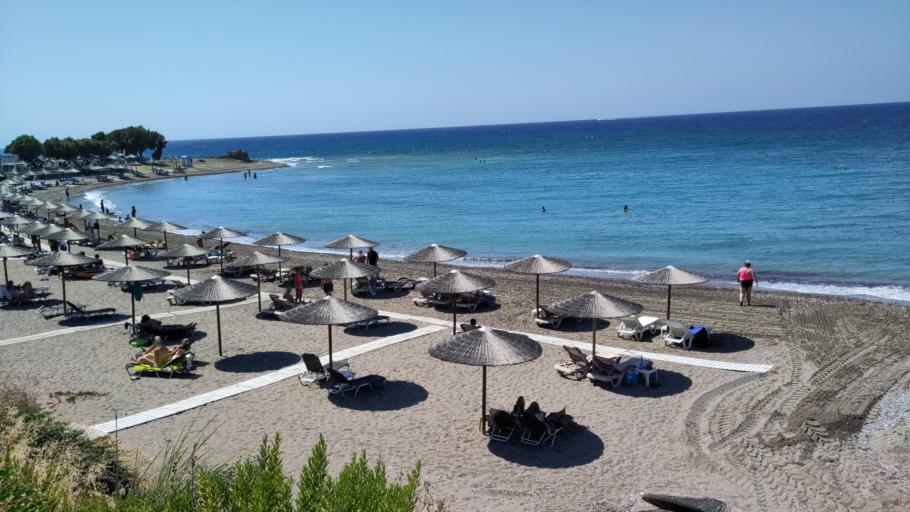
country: GR
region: South Aegean
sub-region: Nomos Dodekanisou
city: Emponas
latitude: 36.3421
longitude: 27.9178
